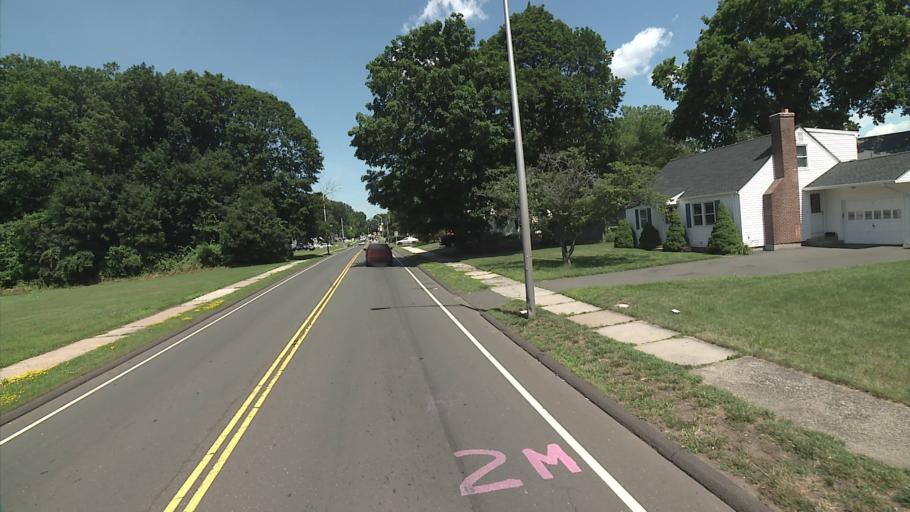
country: US
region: Connecticut
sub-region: Hartford County
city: New Britain
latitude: 41.6591
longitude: -72.8011
